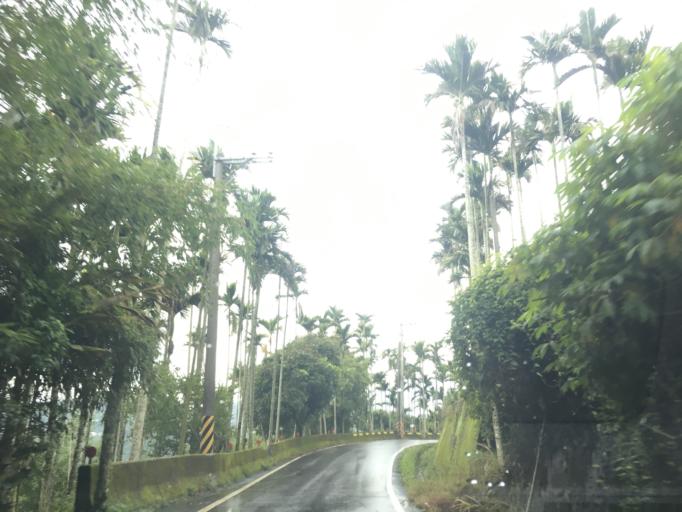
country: TW
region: Taiwan
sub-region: Yunlin
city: Douliu
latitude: 23.5591
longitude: 120.6569
